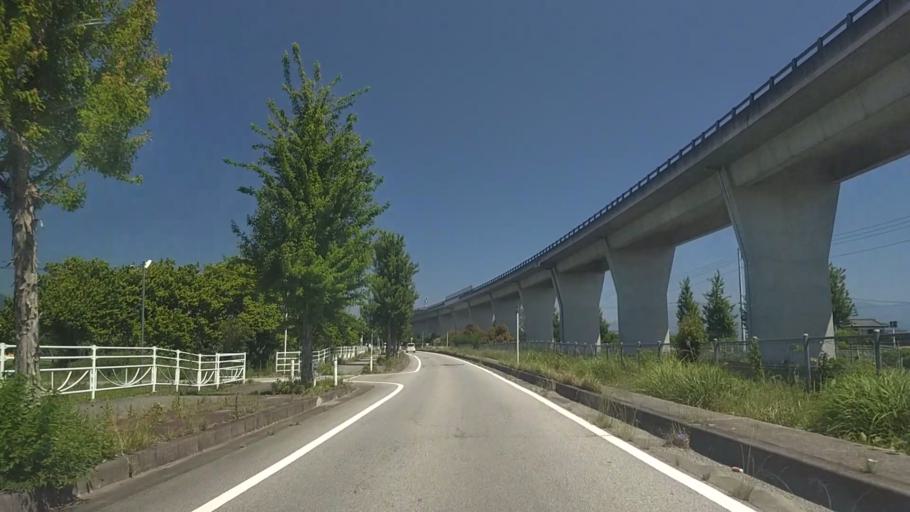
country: JP
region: Yamanashi
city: Ryuo
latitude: 35.6266
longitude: 138.4748
